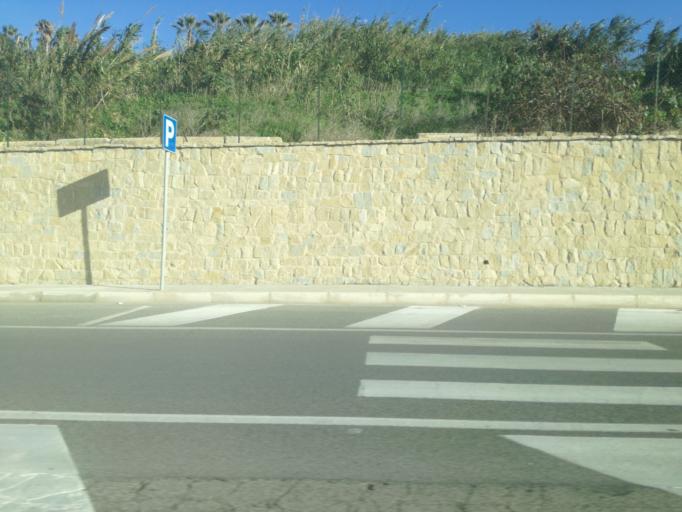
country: IT
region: Sicily
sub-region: Provincia di Caltanissetta
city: Gela
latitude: 37.0673
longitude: 14.2336
